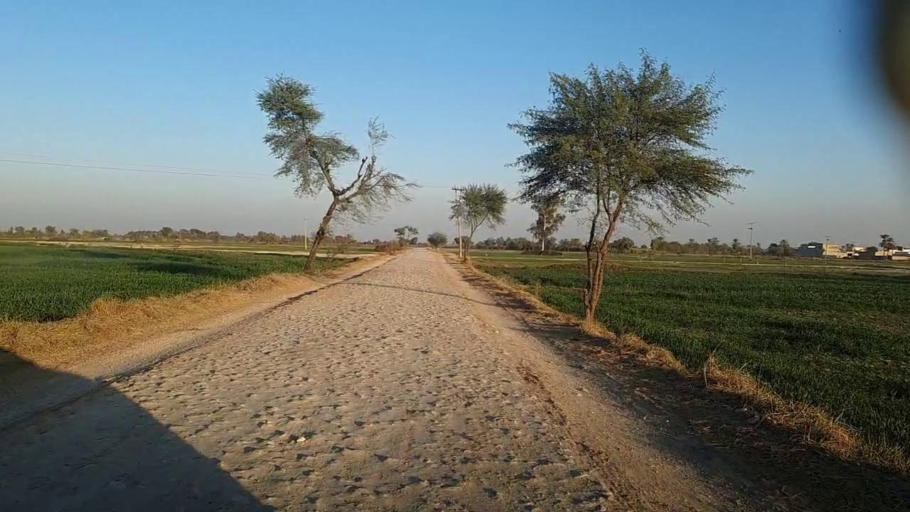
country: PK
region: Sindh
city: Khairpur
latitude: 27.9158
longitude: 69.6853
